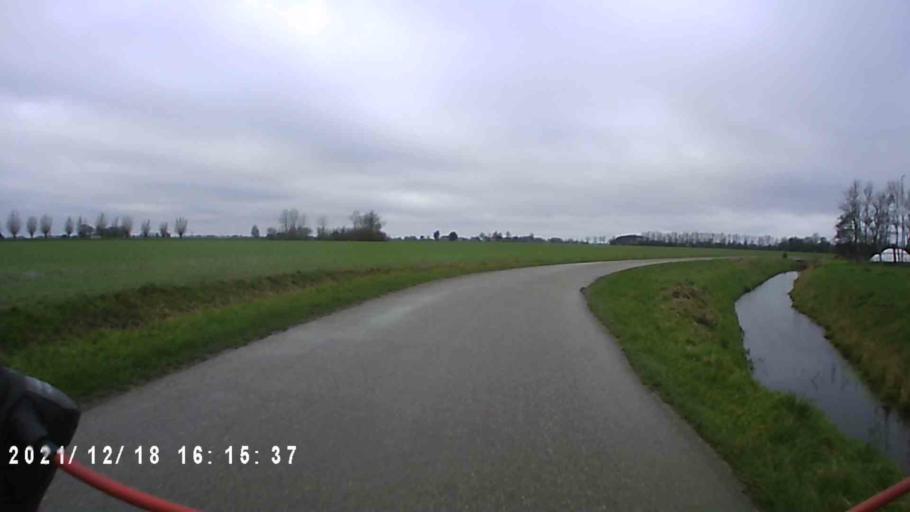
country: NL
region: Friesland
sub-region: Gemeente Dongeradeel
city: Anjum
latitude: 53.3706
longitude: 6.0612
